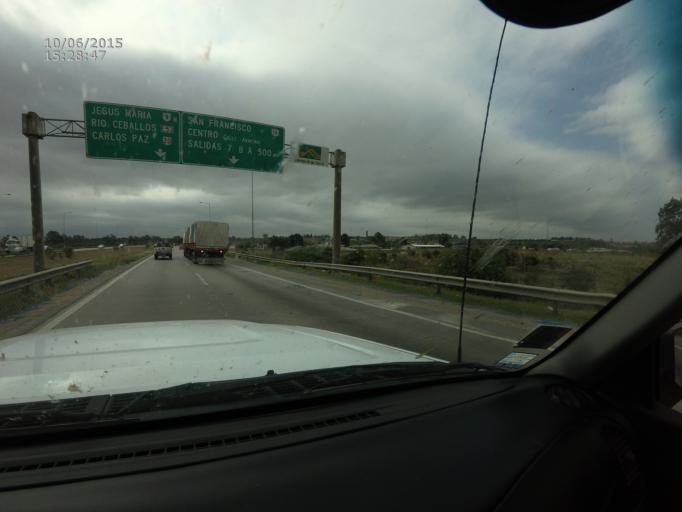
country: AR
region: Cordoba
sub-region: Departamento de Capital
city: Cordoba
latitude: -31.4060
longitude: -64.1241
